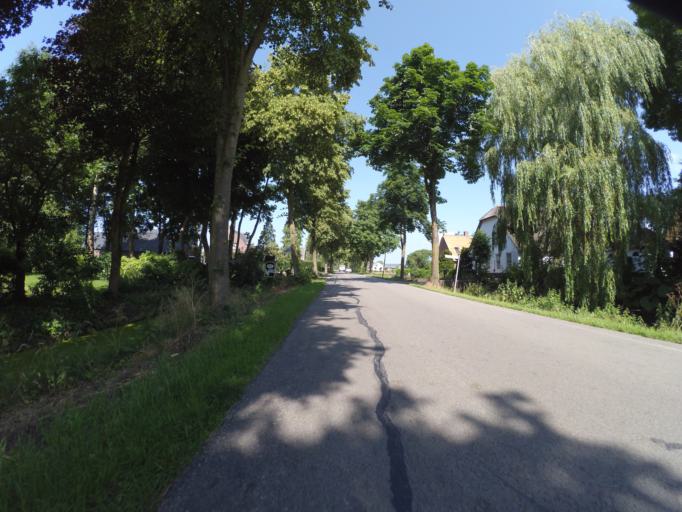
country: NL
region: South Holland
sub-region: Gemeente Leerdam
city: Leerdam
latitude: 51.9386
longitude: 5.1034
